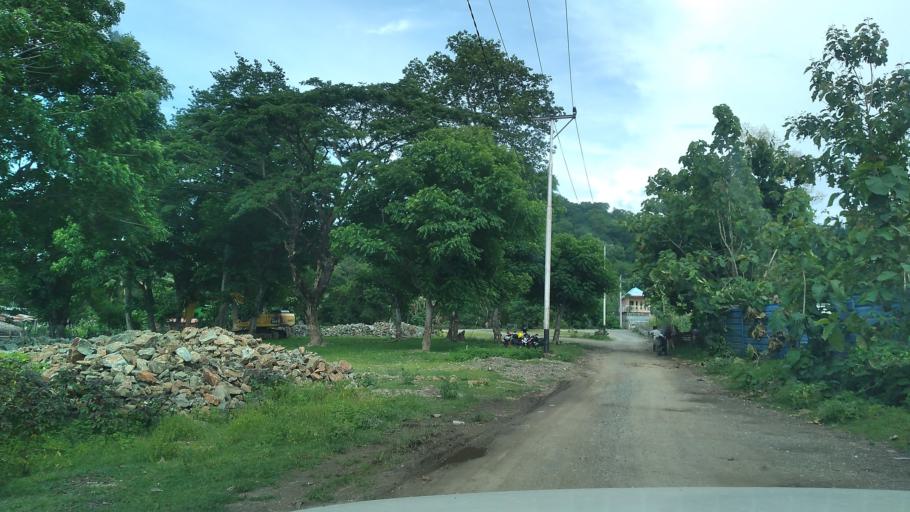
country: TL
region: Dili
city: Dili
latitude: -8.5982
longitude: 125.4815
